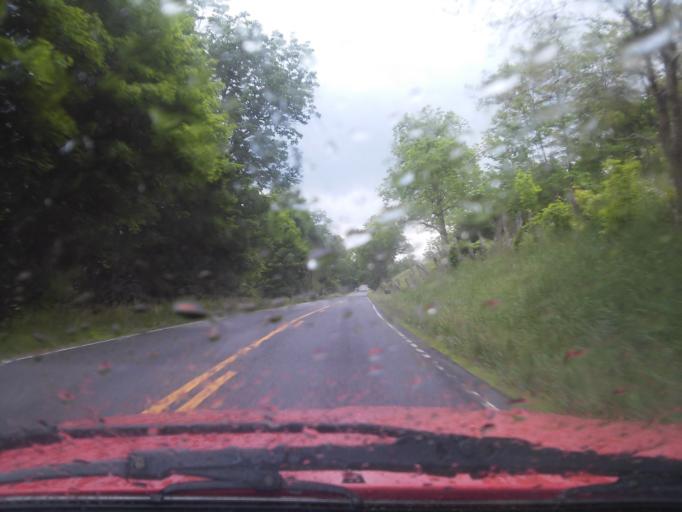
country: US
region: Virginia
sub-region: Montgomery County
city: Blacksburg
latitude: 37.3883
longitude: -80.3599
